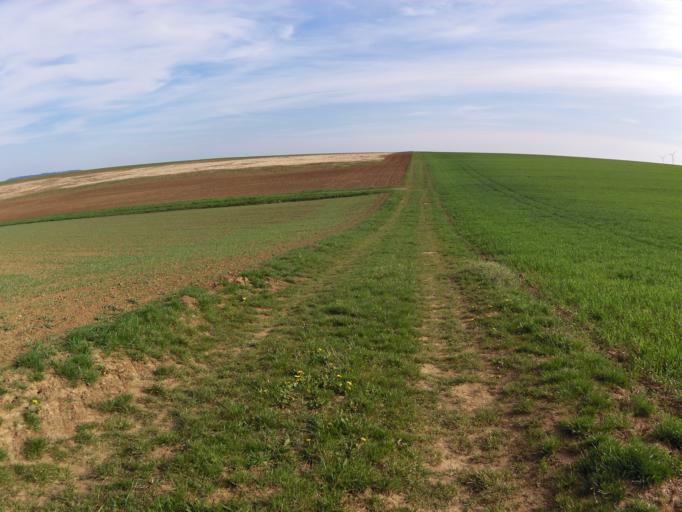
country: DE
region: Bavaria
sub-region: Regierungsbezirk Unterfranken
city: Mainstockheim
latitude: 49.7937
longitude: 10.1325
